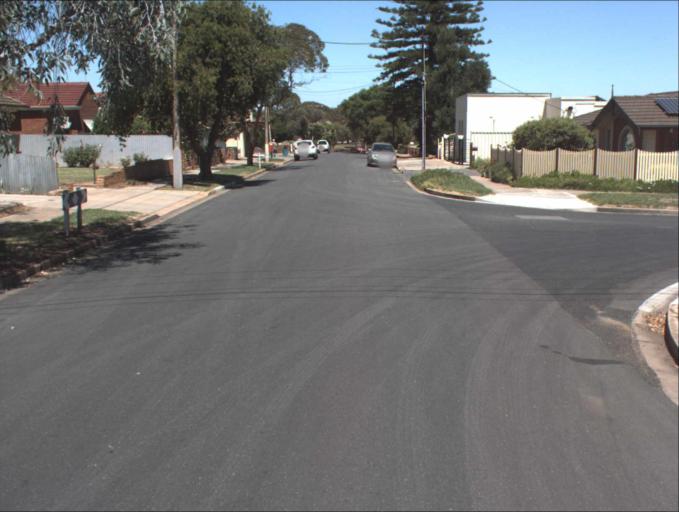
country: AU
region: South Australia
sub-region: Port Adelaide Enfield
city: Enfield
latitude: -34.8627
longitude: 138.6127
